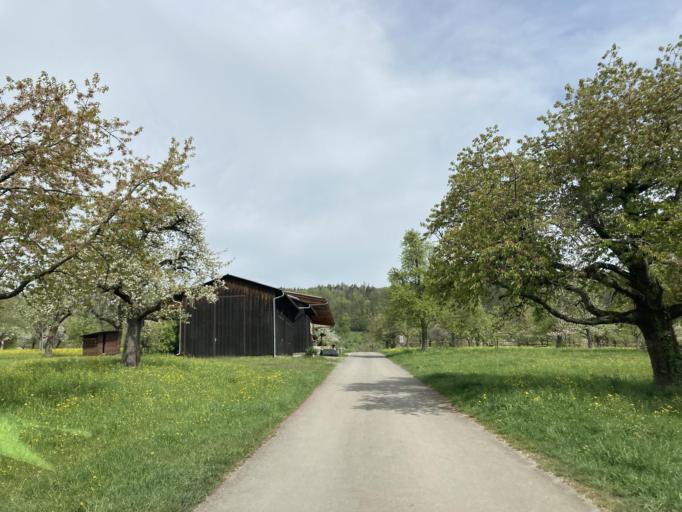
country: DE
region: Baden-Wuerttemberg
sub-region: Regierungsbezirk Stuttgart
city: Hildrizhausen
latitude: 48.5729
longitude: 8.9576
